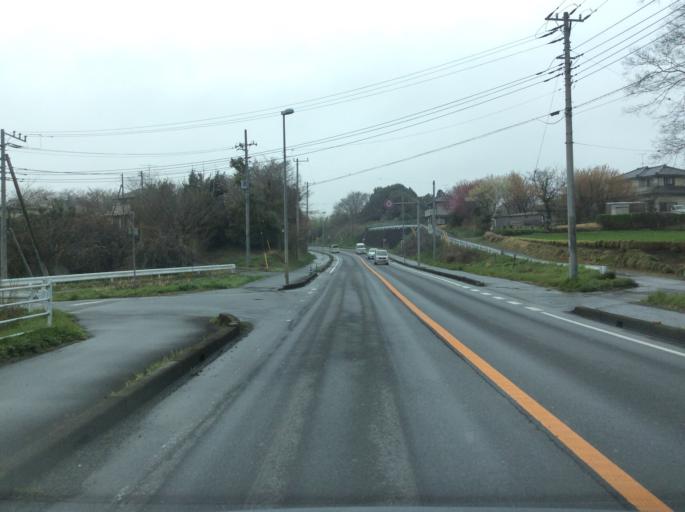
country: JP
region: Ibaraki
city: Mitsukaido
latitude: 35.9913
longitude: 139.9311
